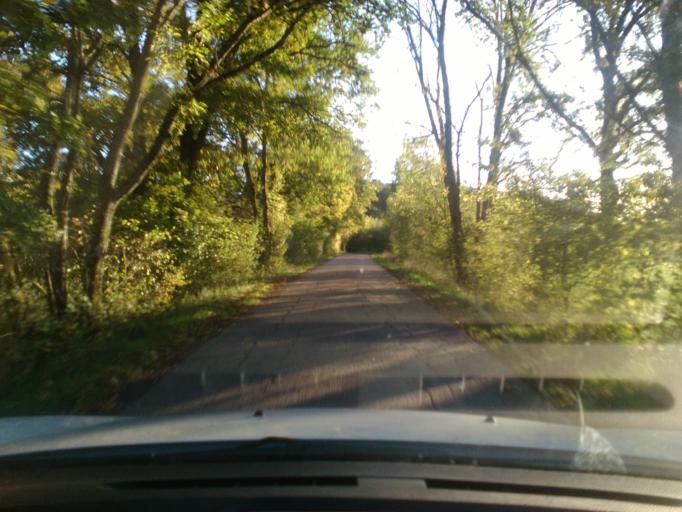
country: FR
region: Lorraine
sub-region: Departement des Vosges
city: Charmes
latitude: 48.3447
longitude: 6.2940
